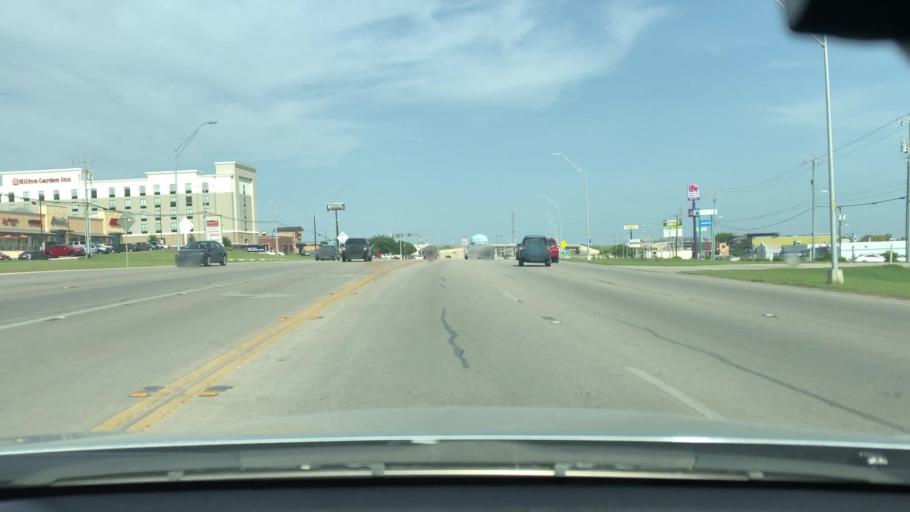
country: US
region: Texas
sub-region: Bexar County
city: Live Oak
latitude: 29.5630
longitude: -98.3334
